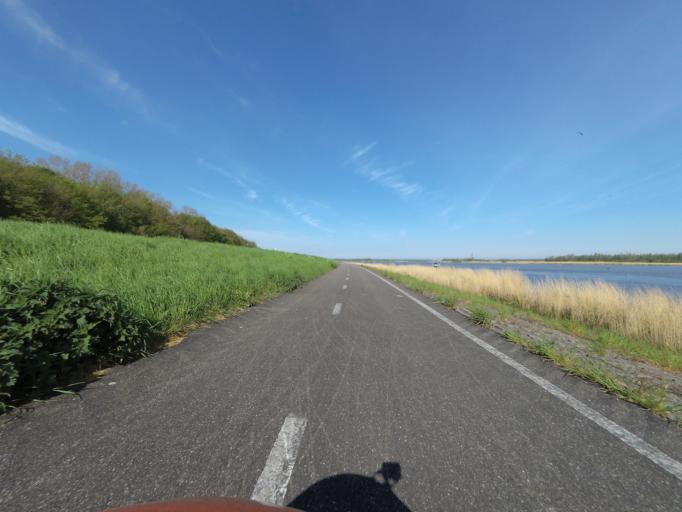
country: NL
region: Flevoland
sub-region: Gemeente Noordoostpolder
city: Ens
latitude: 52.5790
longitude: 5.8083
